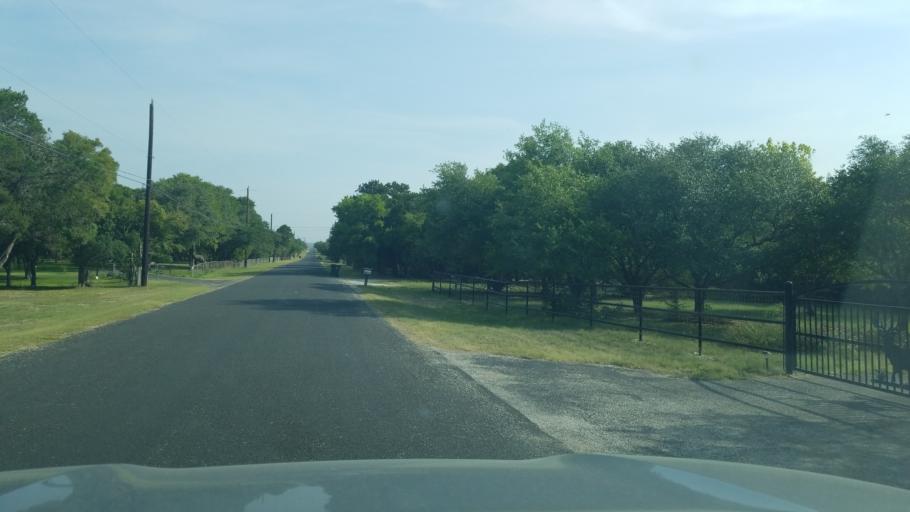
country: US
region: Texas
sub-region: Bexar County
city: Timberwood Park
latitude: 29.7155
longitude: -98.4887
